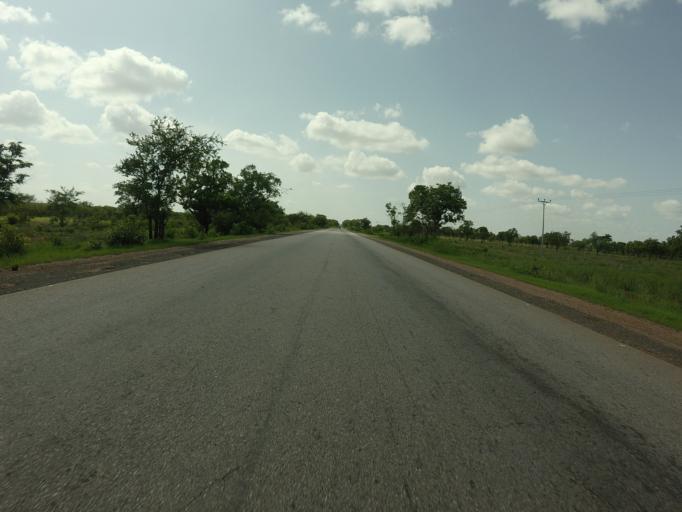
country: GH
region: Northern
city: Savelugu
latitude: 9.8251
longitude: -0.8640
